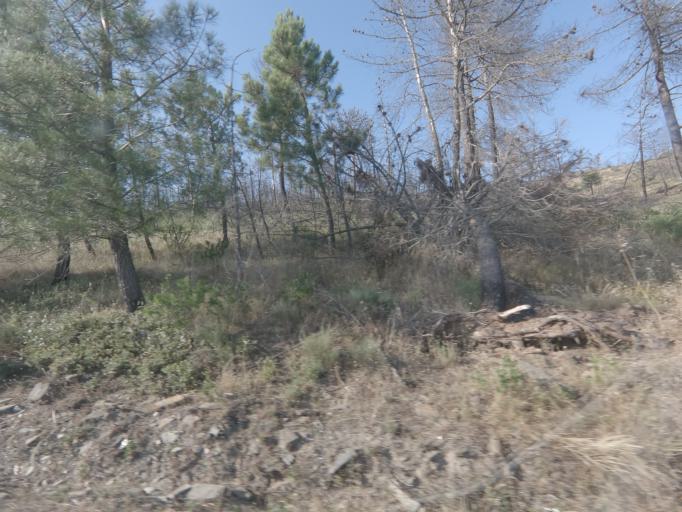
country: PT
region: Vila Real
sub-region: Sabrosa
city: Vilela
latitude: 41.1870
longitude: -7.6163
